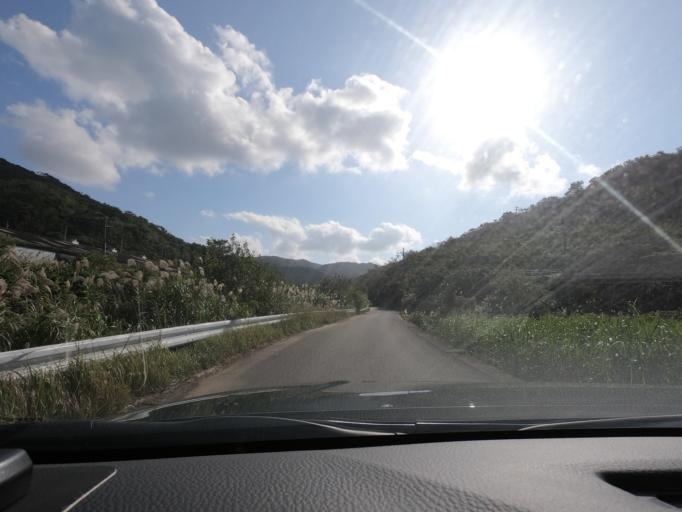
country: JP
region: Okinawa
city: Nago
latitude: 26.7661
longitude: 128.2095
